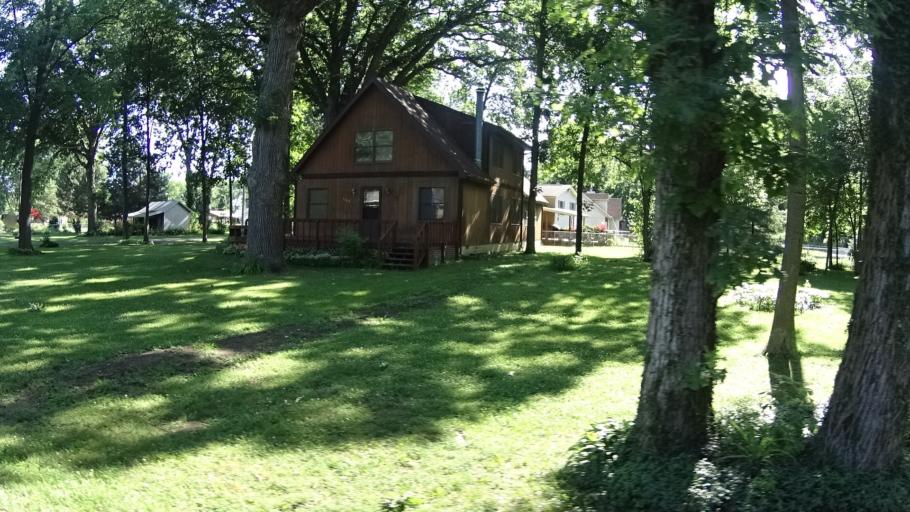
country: US
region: Ohio
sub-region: Erie County
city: Sandusky
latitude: 41.4646
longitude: -82.8253
